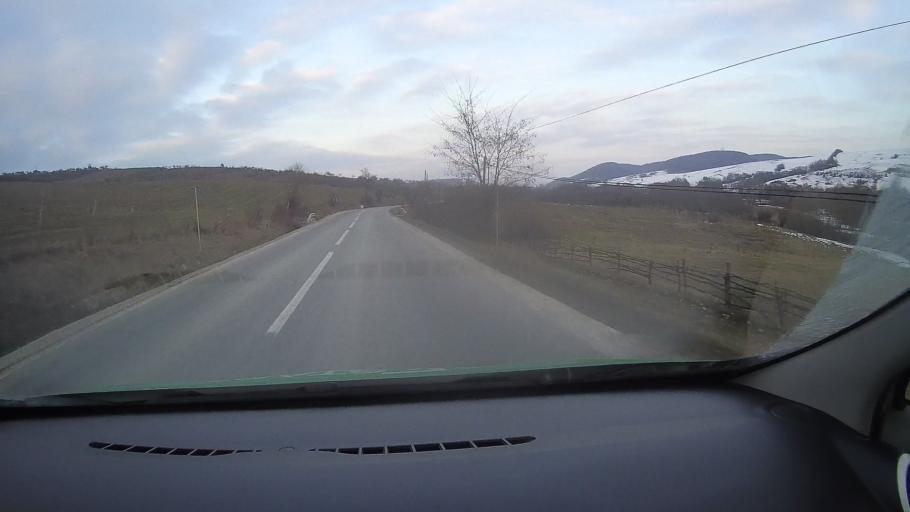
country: RO
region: Harghita
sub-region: Comuna Simonesti
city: Simonesti
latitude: 46.3570
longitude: 25.1580
